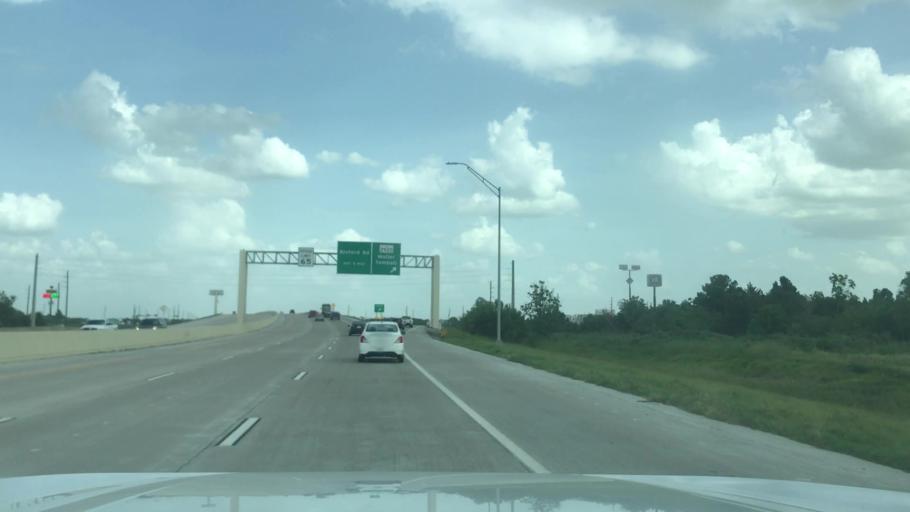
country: US
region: Texas
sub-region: Waller County
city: Waller
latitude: 30.0651
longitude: -95.9138
